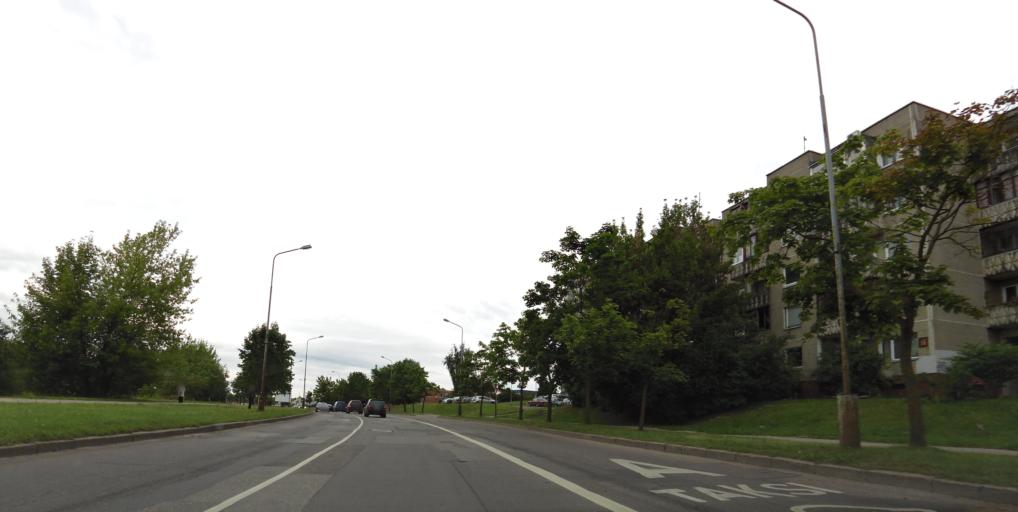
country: LT
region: Vilnius County
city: Seskine
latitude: 54.7131
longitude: 25.2562
